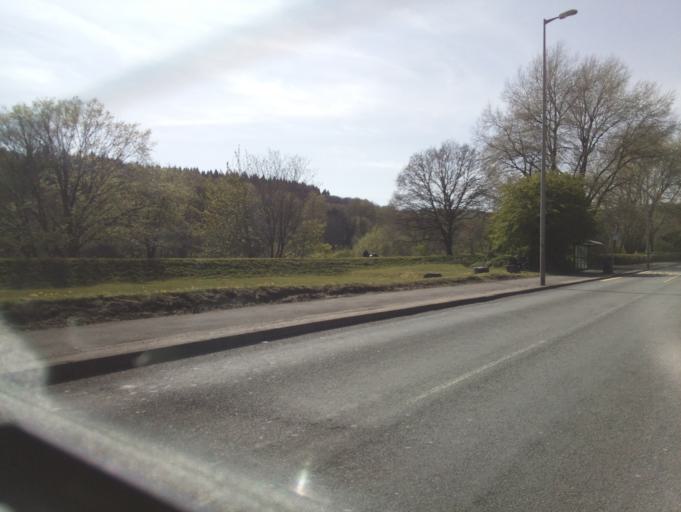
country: GB
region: Wales
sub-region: Caerphilly County Borough
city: Abertridwr
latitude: 51.5618
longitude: -3.2765
